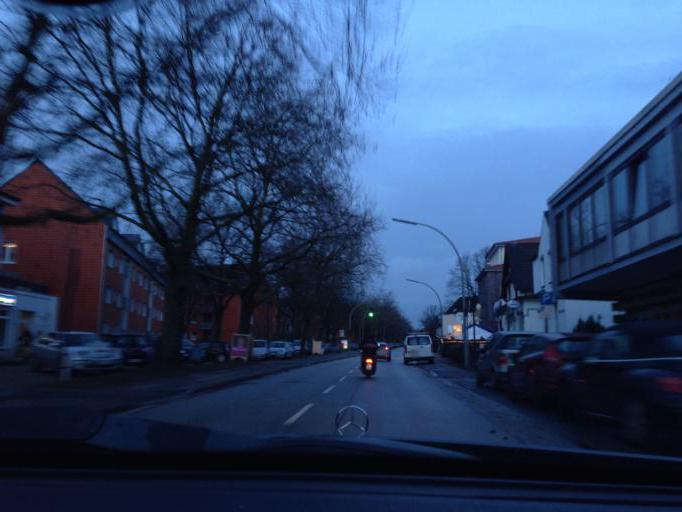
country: DE
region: Hamburg
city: Farmsen-Berne
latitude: 53.6028
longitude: 10.1296
